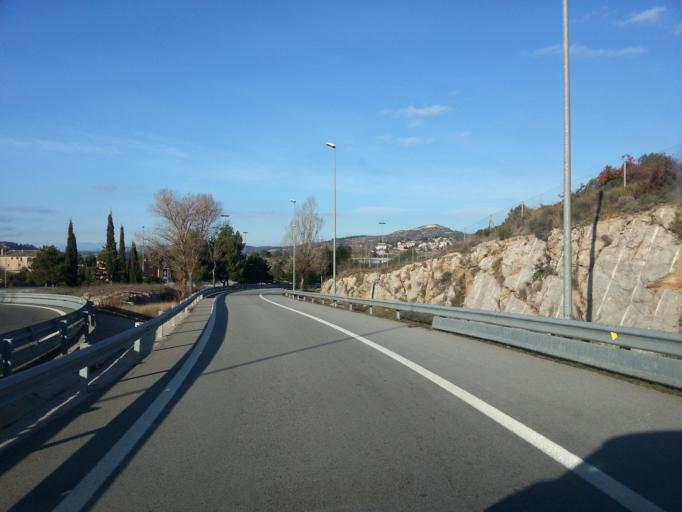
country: ES
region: Catalonia
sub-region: Provincia de Barcelona
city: Monistrol de Montserrat
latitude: 41.6496
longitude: 1.8643
